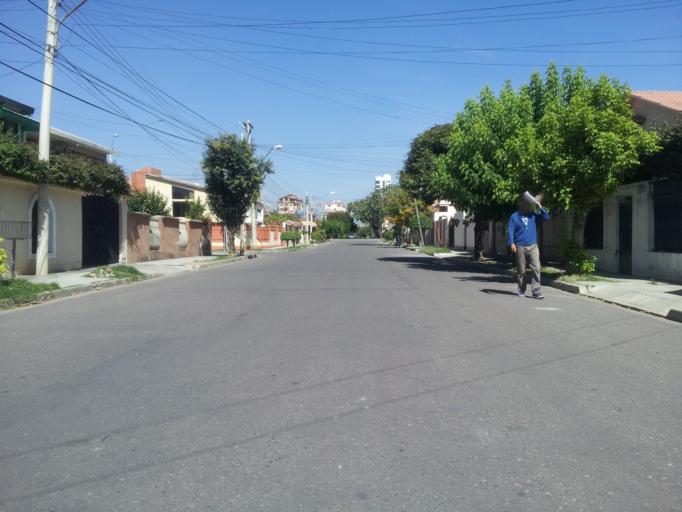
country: BO
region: Cochabamba
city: Cochabamba
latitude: -17.3782
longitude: -66.1722
